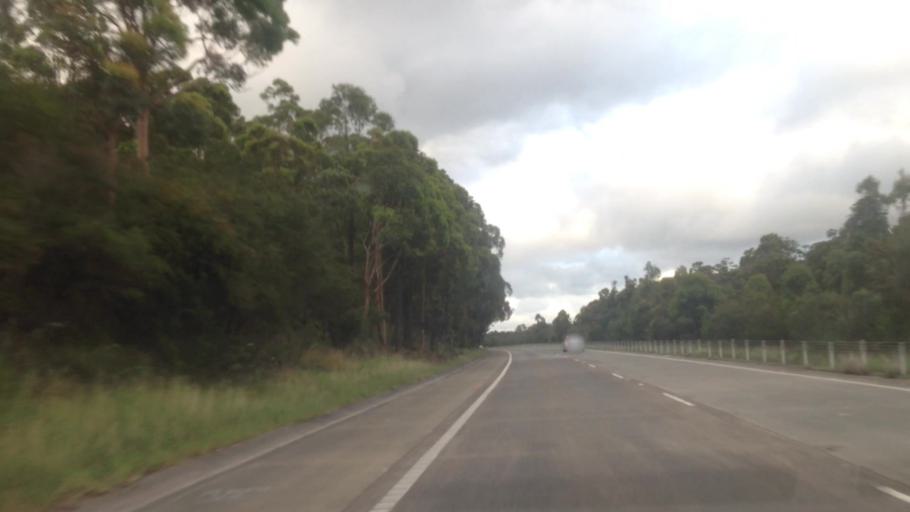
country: AU
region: New South Wales
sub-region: Wyong Shire
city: Charmhaven
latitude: -33.2005
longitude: 151.4619
